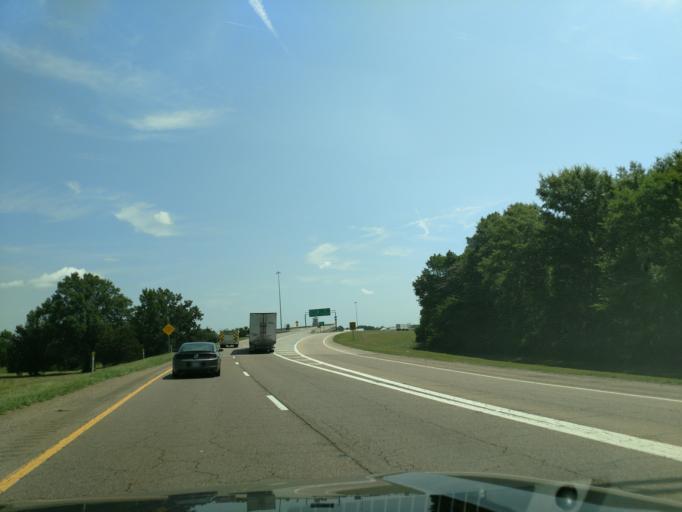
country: US
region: Mississippi
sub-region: Rankin County
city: Pearl
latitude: 32.2689
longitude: -90.1593
